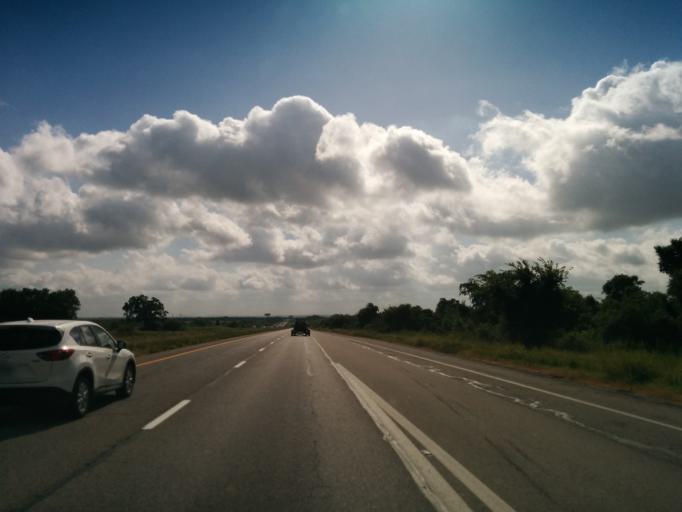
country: US
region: Texas
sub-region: Caldwell County
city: Luling
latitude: 29.6466
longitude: -97.6909
